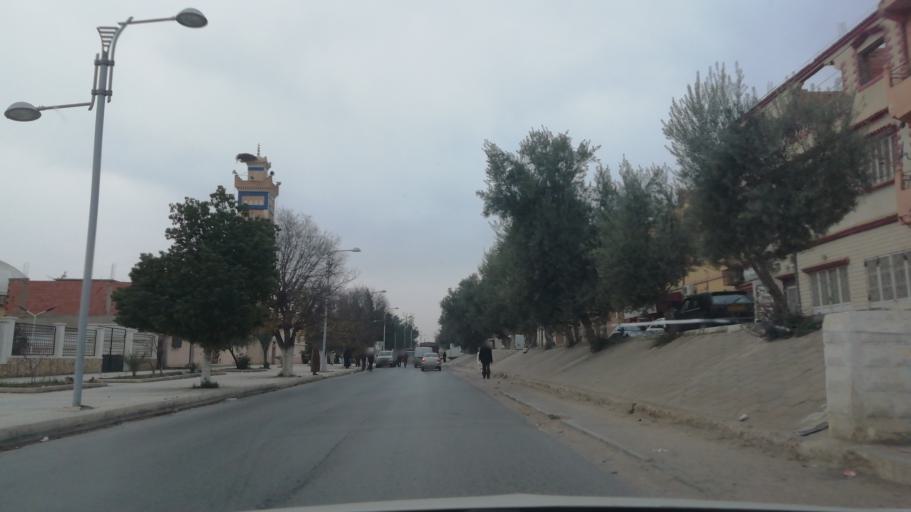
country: DZ
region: Sidi Bel Abbes
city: Sfizef
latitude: 35.2384
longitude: -0.2361
